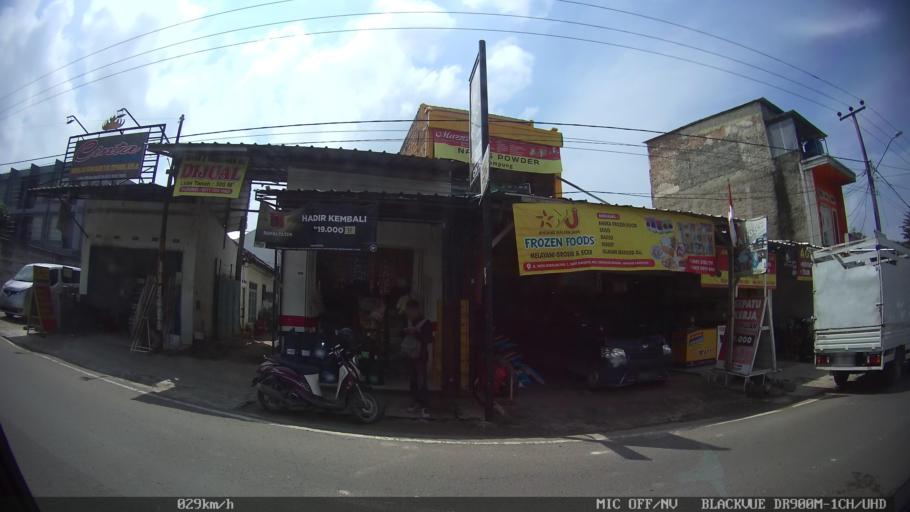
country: ID
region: Lampung
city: Kedaton
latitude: -5.3498
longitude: 105.2931
